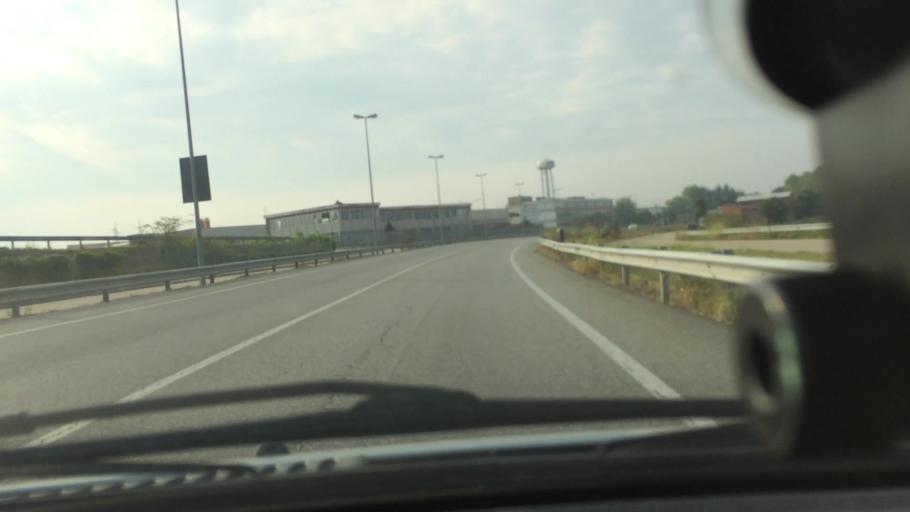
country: IT
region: Piedmont
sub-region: Provincia di Torino
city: Villastellone
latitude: 44.9157
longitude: 7.7428
